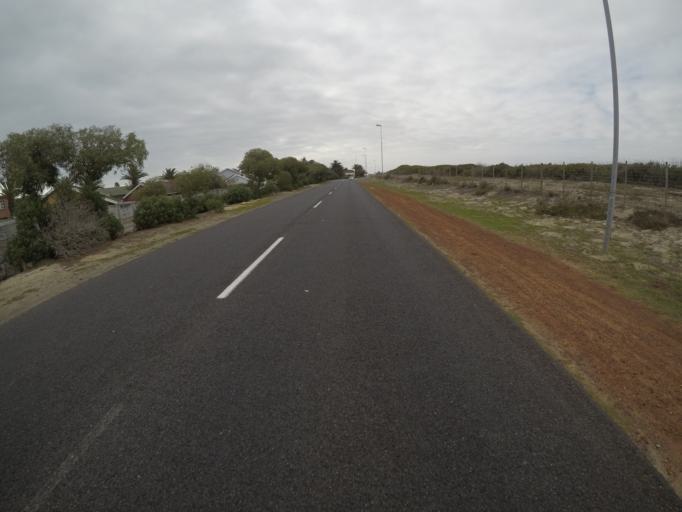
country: ZA
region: Western Cape
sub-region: City of Cape Town
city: Atlantis
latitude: -33.6985
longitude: 18.4447
